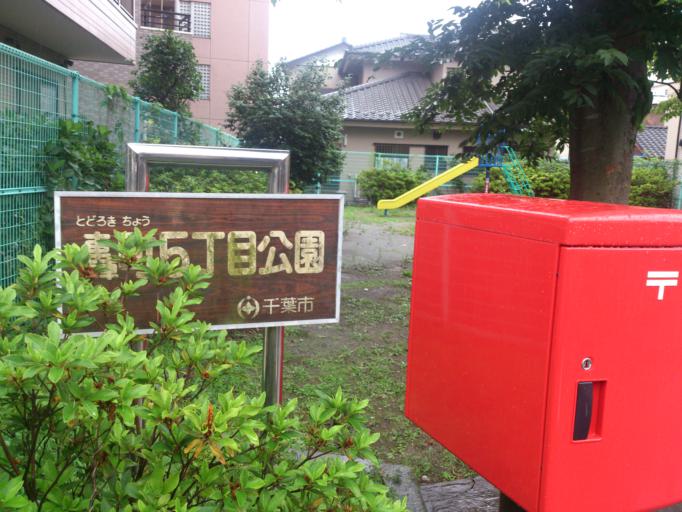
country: JP
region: Chiba
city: Chiba
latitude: 35.6329
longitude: 140.1118
